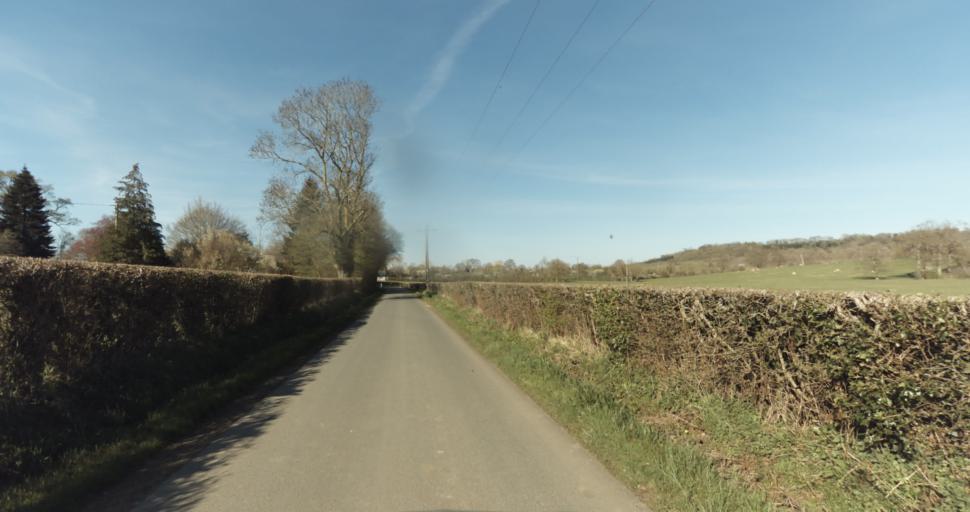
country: FR
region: Lower Normandy
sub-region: Departement du Calvados
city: Saint-Pierre-sur-Dives
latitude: 49.0254
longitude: 0.0557
